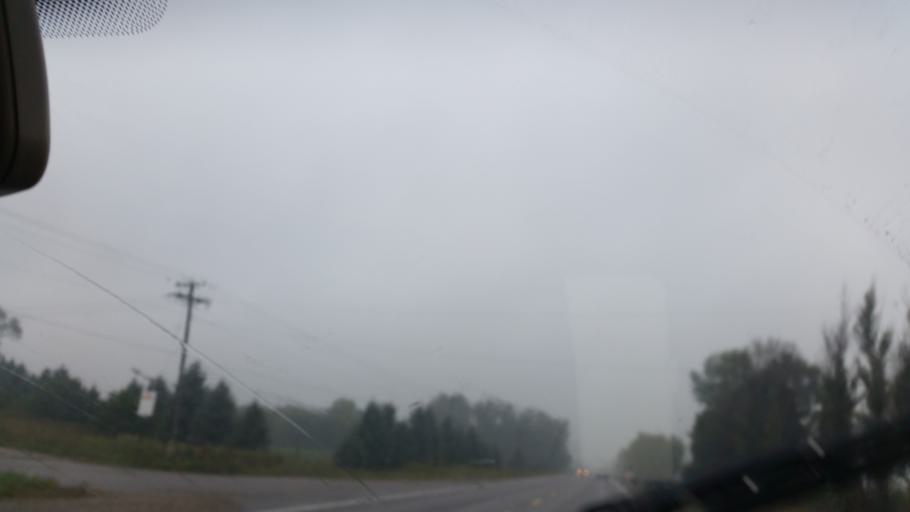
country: CA
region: Ontario
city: Stratford
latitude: 43.2855
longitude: -81.0550
